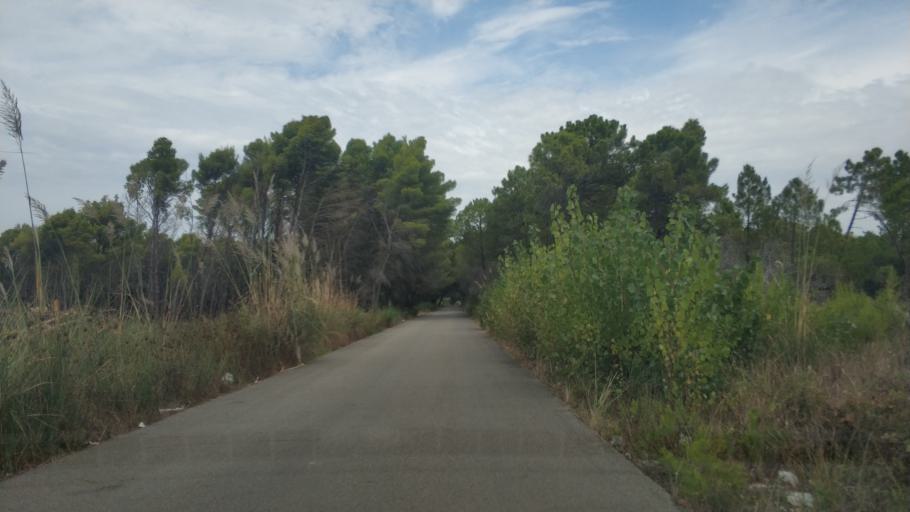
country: AL
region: Vlore
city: Vlore
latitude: 40.4941
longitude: 19.4346
